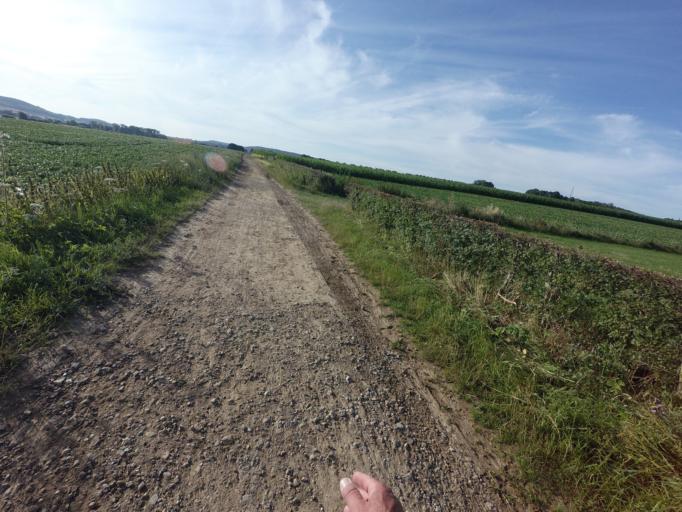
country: NL
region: Limburg
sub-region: Gemeente Simpelveld
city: Simpelveld
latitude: 50.7880
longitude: 5.9715
